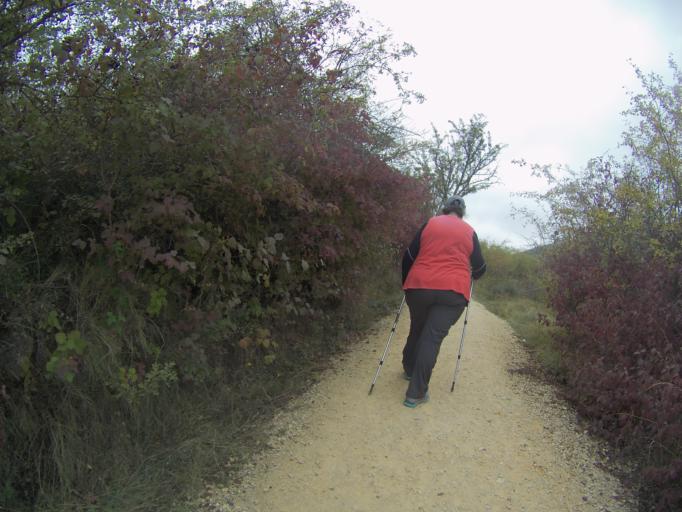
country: ES
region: Navarre
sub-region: Provincia de Navarra
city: Villamayor de Monjardin
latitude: 42.6323
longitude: -2.0937
